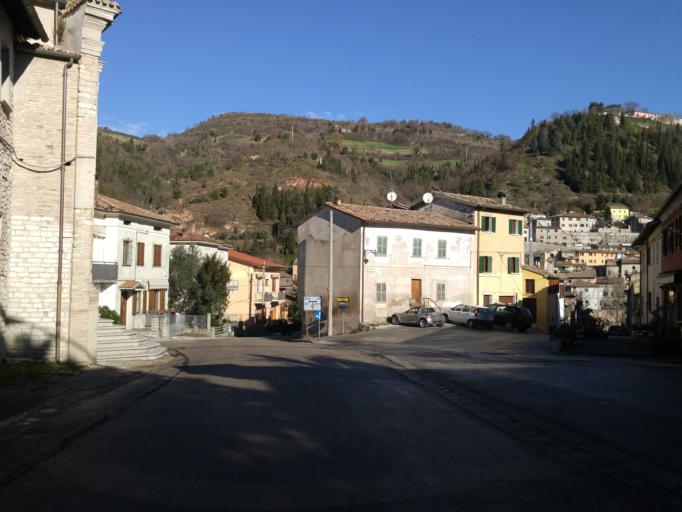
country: IT
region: The Marches
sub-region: Provincia di Pesaro e Urbino
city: Fossombrone
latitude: 43.6863
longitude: 12.8032
